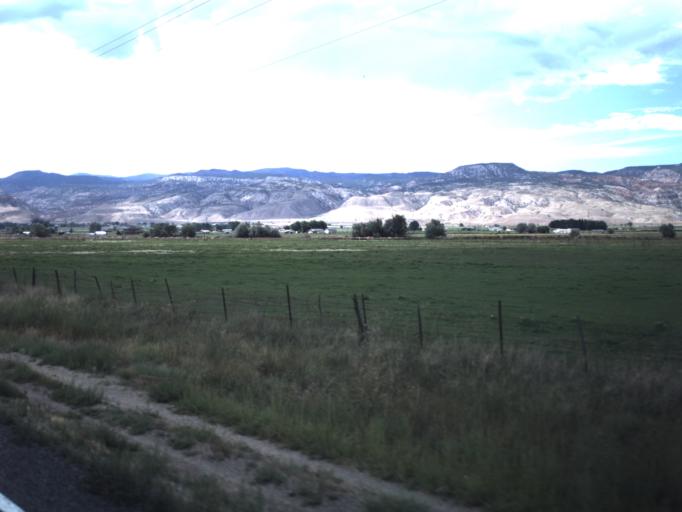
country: US
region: Utah
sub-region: Sevier County
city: Richfield
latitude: 38.7736
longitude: -112.0363
